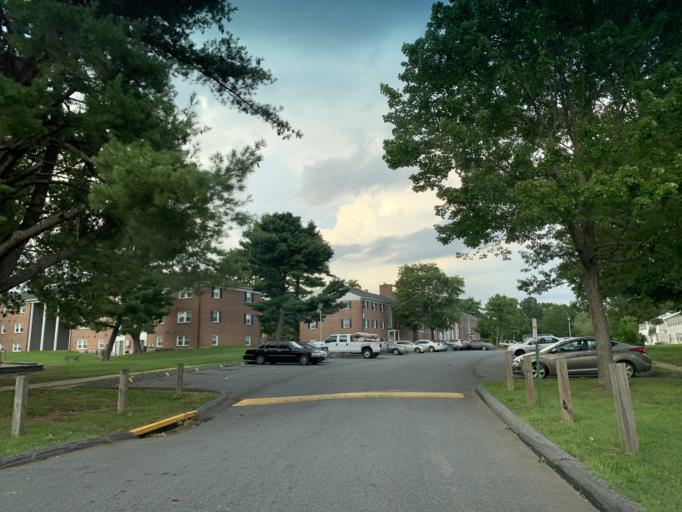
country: US
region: Maryland
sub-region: Baltimore County
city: Essex
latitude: 39.3024
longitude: -76.4470
